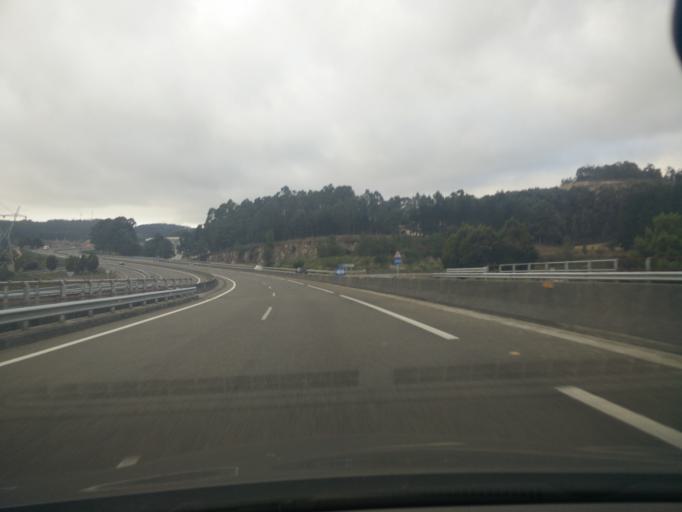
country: ES
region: Galicia
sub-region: Provincia da Coruna
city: Arteixo
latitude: 43.3064
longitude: -8.4745
